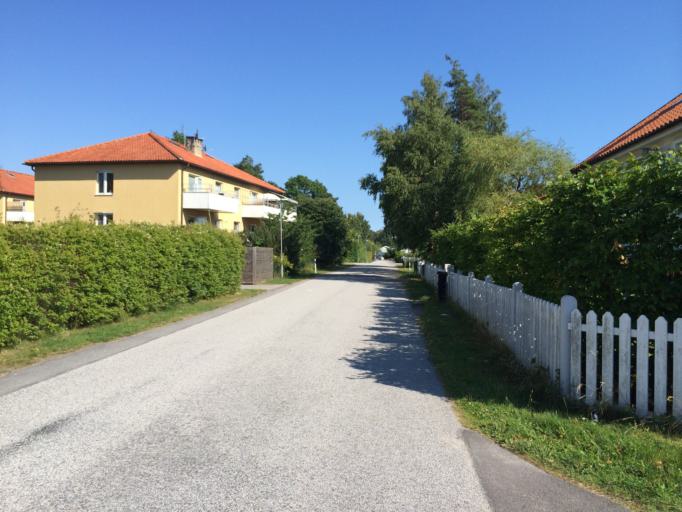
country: SE
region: Skane
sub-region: Vellinge Kommun
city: Skanor med Falsterbo
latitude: 55.4080
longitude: 12.8432
